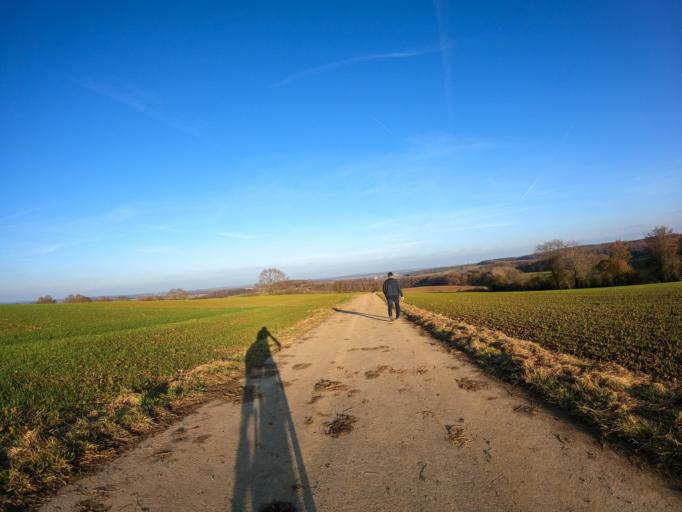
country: LU
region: Luxembourg
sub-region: Canton de Capellen
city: Garnich
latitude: 49.6023
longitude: 5.9581
